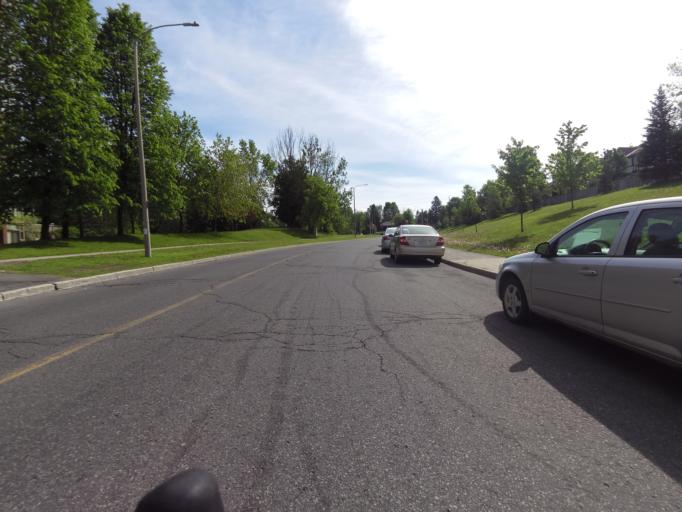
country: CA
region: Ontario
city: Ottawa
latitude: 45.3500
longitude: -75.6430
